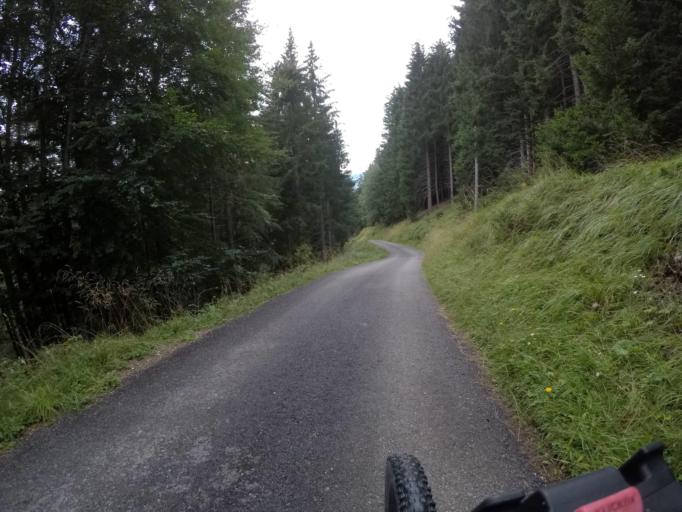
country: IT
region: Friuli Venezia Giulia
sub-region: Provincia di Udine
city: Pontebba
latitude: 46.5144
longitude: 13.2440
